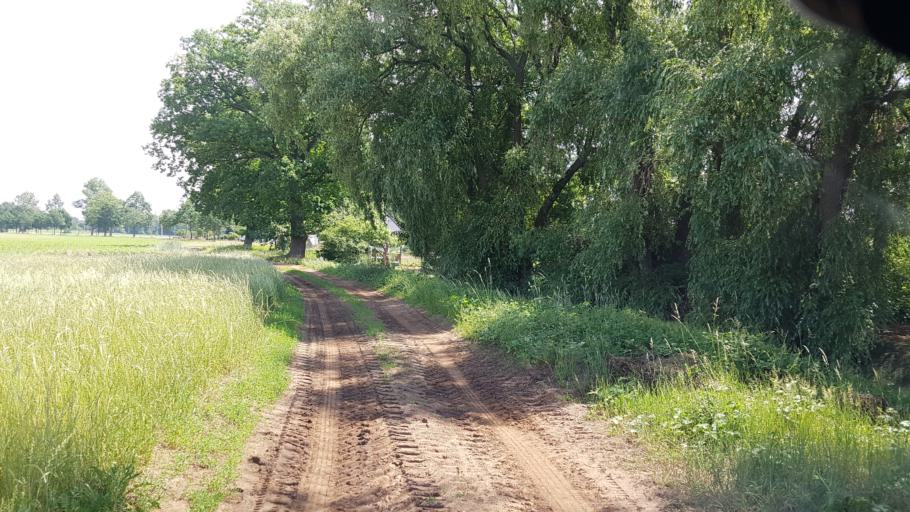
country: DE
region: Brandenburg
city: Ruckersdorf
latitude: 51.5978
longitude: 13.6127
